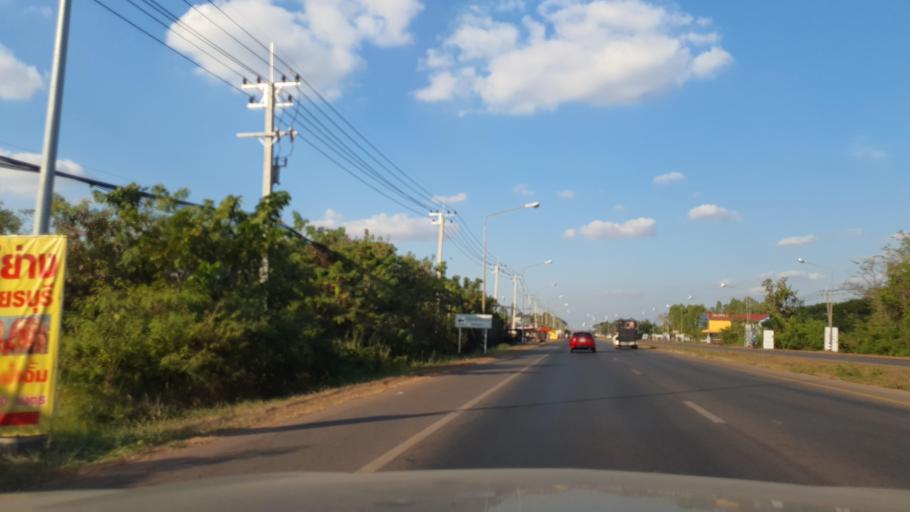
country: TH
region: Sakon Nakhon
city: Sakon Nakhon
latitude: 17.2115
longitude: 104.1025
